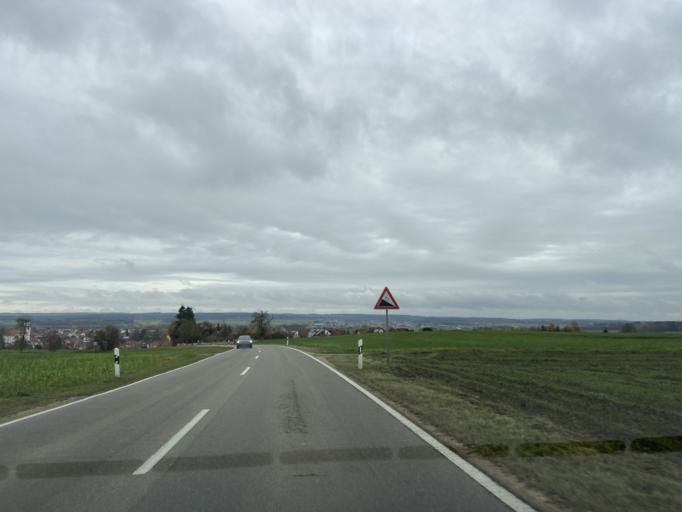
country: DE
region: Baden-Wuerttemberg
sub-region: Tuebingen Region
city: Messkirch
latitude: 47.9895
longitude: 9.1254
